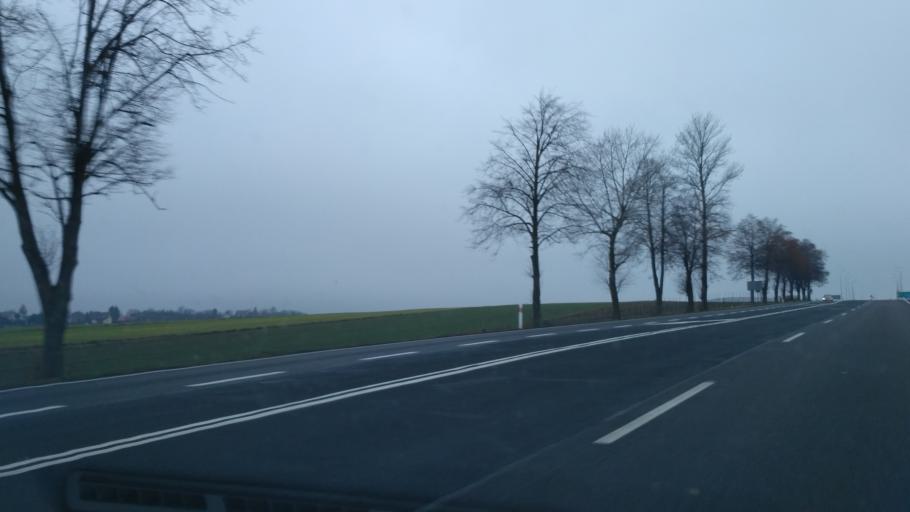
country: PL
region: Subcarpathian Voivodeship
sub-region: Powiat jaroslawski
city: Wierzbna
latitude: 50.0342
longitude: 22.5934
